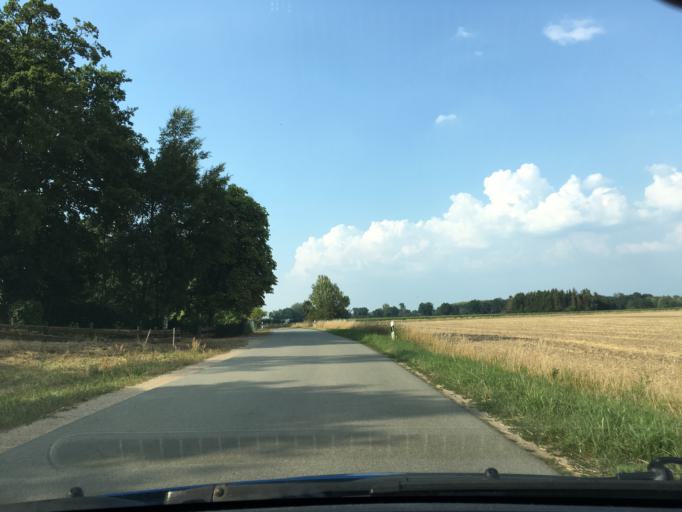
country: DE
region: Lower Saxony
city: Damnatz
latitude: 53.1423
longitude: 11.1225
